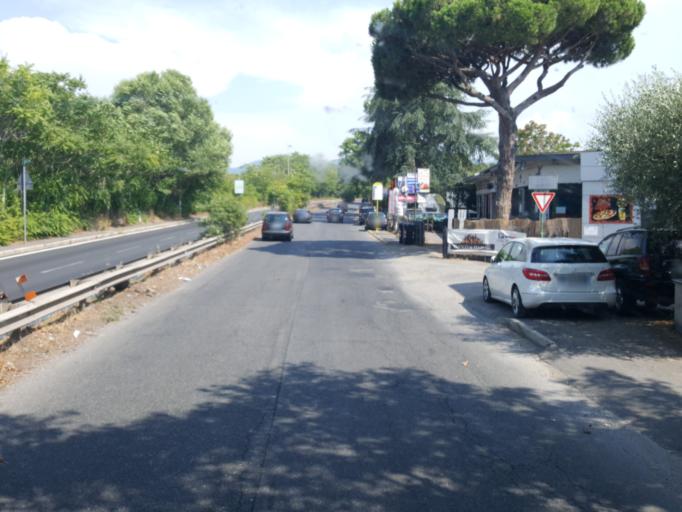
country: IT
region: Latium
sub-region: Citta metropolitana di Roma Capitale
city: Ciampino
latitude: 41.8271
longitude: 12.6258
